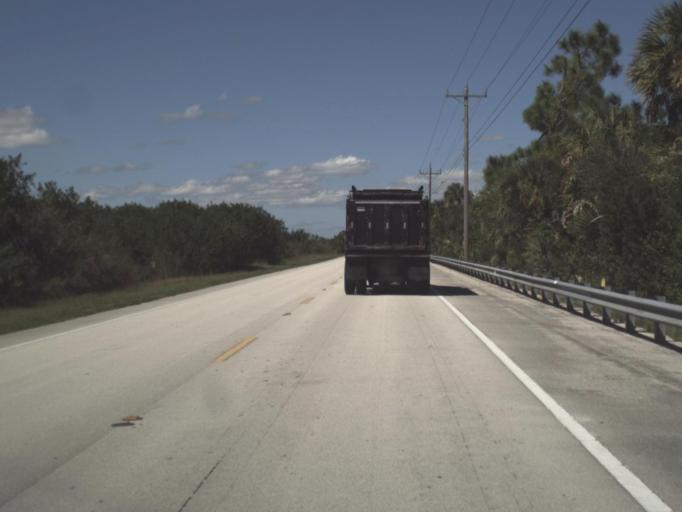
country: US
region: Florida
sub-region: Collier County
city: Marco
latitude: 25.9628
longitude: -81.5215
